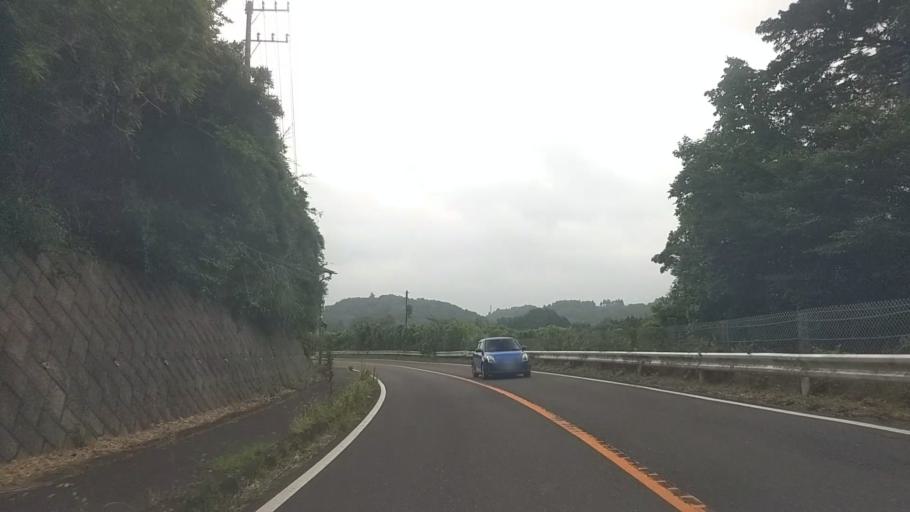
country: JP
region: Chiba
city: Kawaguchi
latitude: 35.2624
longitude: 140.0585
